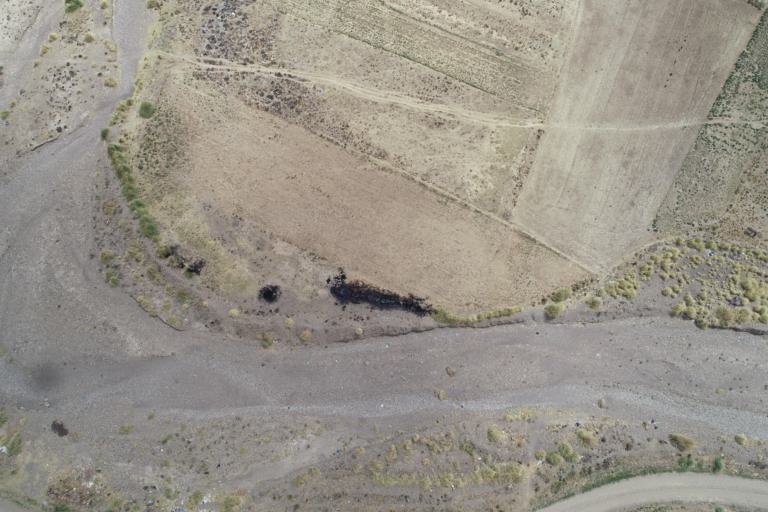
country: BO
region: La Paz
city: Achacachi
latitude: -15.9150
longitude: -68.8844
